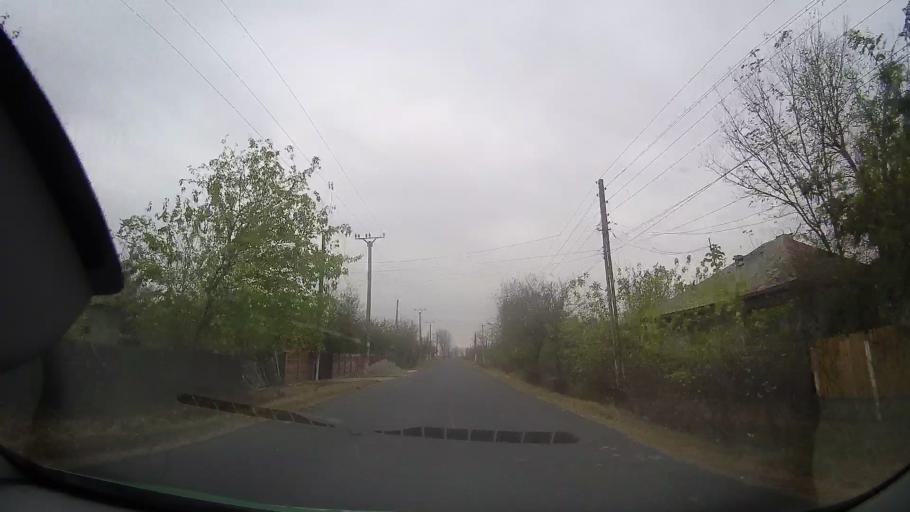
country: RO
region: Braila
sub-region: Comuna Ciresu
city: Ciresu
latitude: 44.9402
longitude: 27.3597
